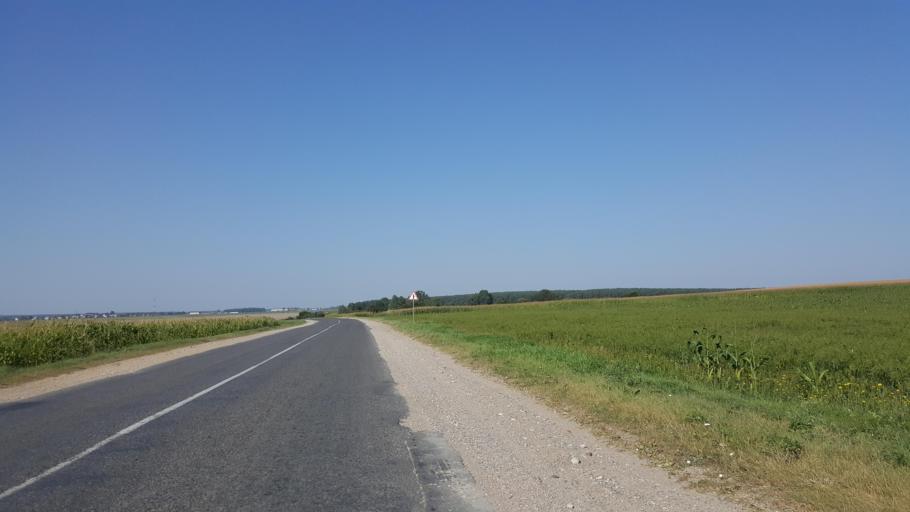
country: BY
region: Brest
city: Kamyanyets
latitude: 52.4177
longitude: 23.6713
